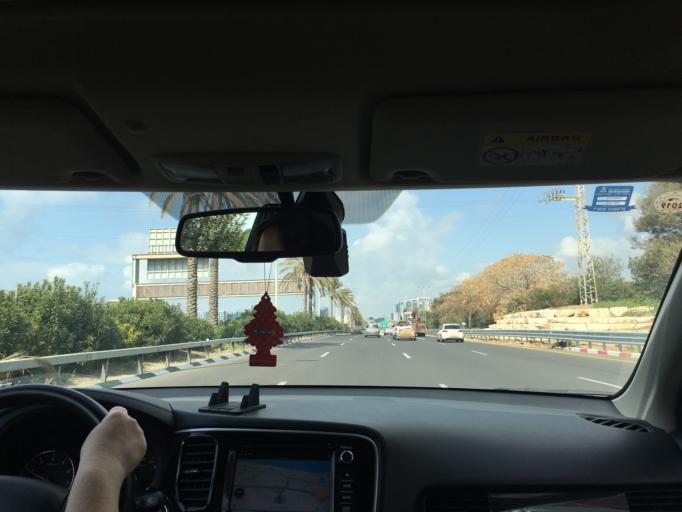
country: IL
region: Tel Aviv
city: Herzliya Pituah
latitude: 32.1503
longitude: 34.8049
